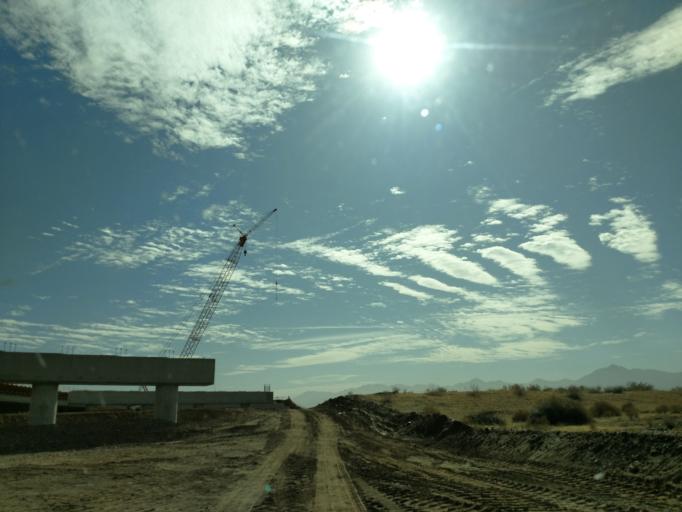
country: US
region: Arizona
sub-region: Maricopa County
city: Laveen
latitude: 33.3991
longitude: -112.1926
